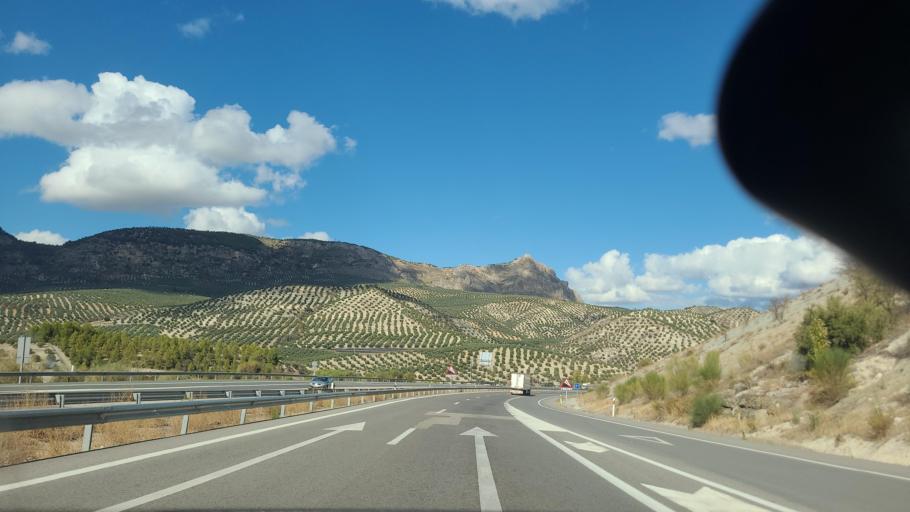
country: ES
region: Andalusia
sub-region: Provincia de Jaen
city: Campillo de Arenas
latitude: 37.5595
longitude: -3.6257
